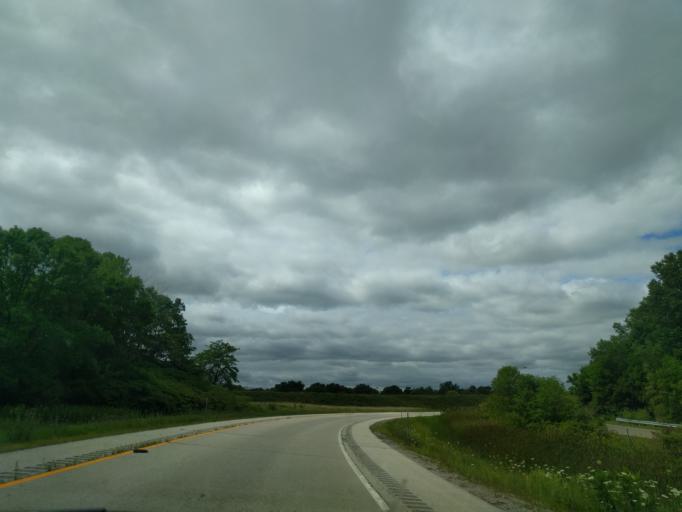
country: US
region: Wisconsin
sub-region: Brown County
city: Ashwaubenon
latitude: 44.4883
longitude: -88.0837
